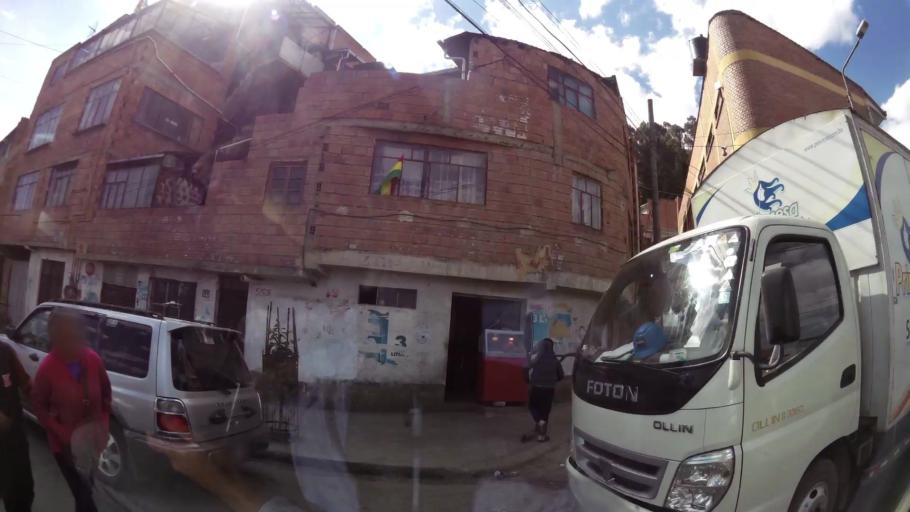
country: BO
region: La Paz
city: La Paz
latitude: -16.4871
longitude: -68.1323
